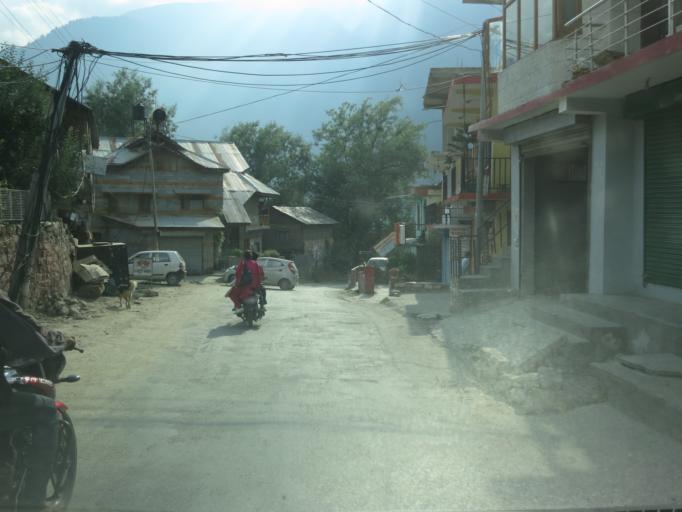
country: IN
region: Himachal Pradesh
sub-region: Kulu
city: Manali
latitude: 32.1980
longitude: 77.2023
